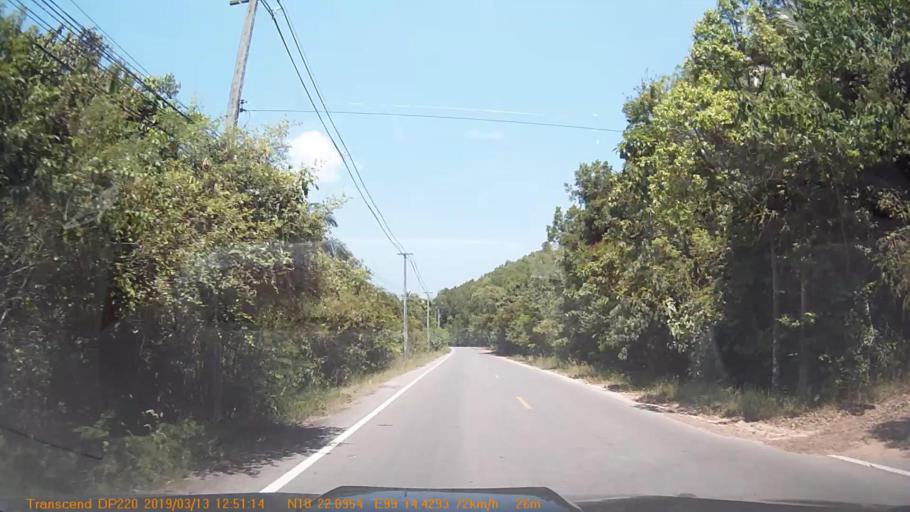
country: TH
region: Chumphon
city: Chumphon
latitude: 10.3686
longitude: 99.2406
